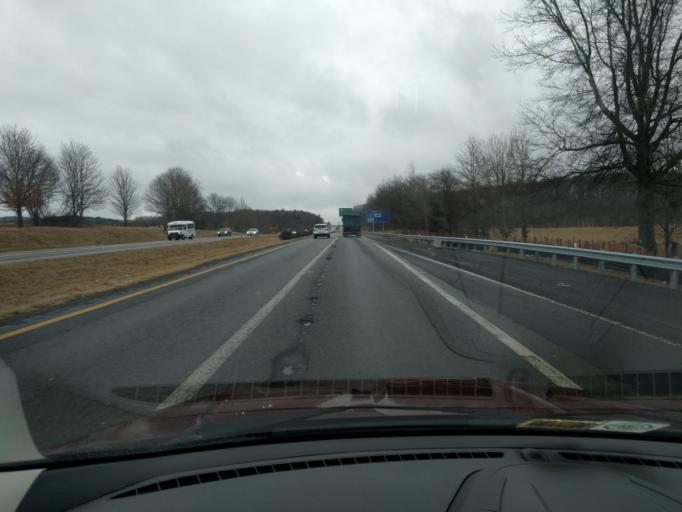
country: US
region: Virginia
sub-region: Montgomery County
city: Merrimac
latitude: 37.2058
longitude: -80.4219
